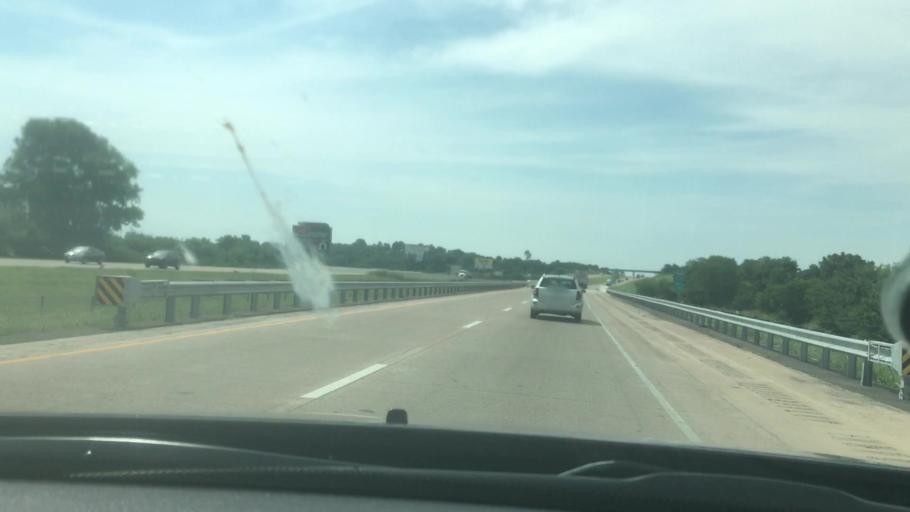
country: US
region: Oklahoma
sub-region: Garvin County
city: Pauls Valley
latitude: 34.7333
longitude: -97.2587
